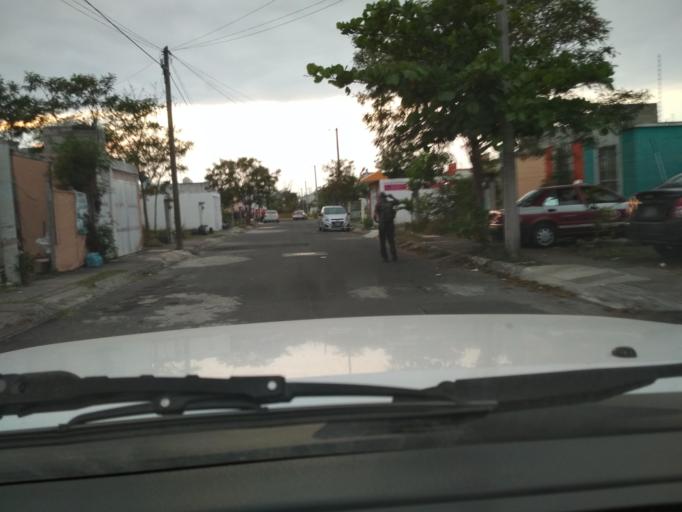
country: MX
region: Veracruz
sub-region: Medellin
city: Fraccionamiento Arboledas San Ramon
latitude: 19.0920
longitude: -96.1599
